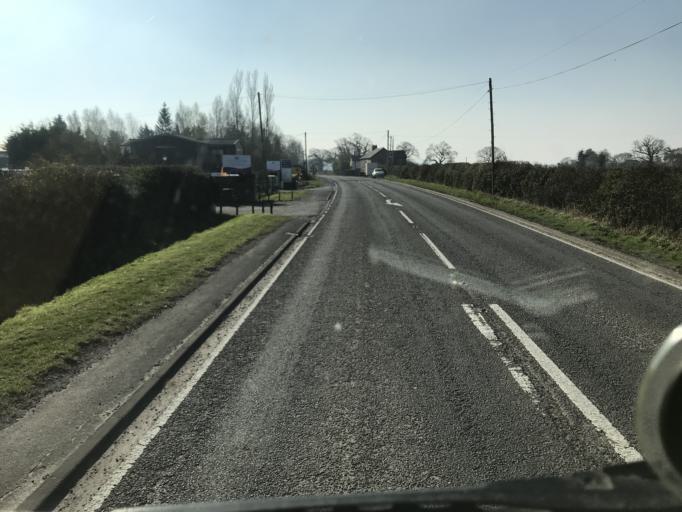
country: GB
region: England
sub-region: Cheshire West and Chester
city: Waverton
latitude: 53.1425
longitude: -2.8119
